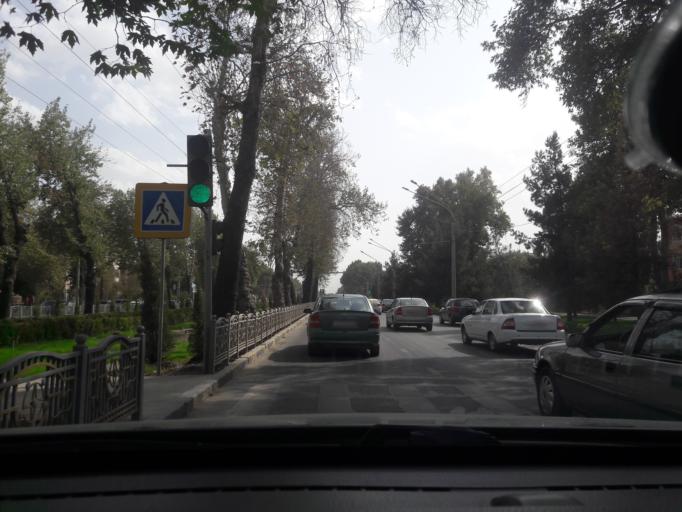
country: TJ
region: Dushanbe
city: Dushanbe
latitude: 38.5478
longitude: 68.7619
